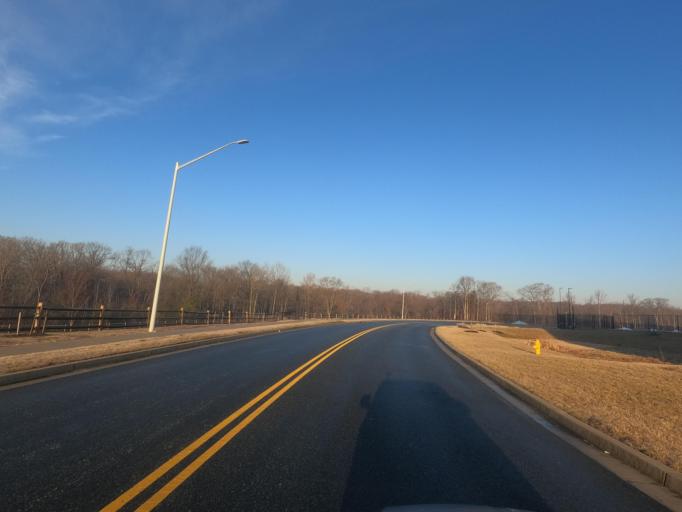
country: US
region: Maryland
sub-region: Cecil County
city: North East
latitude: 39.6126
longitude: -75.9508
